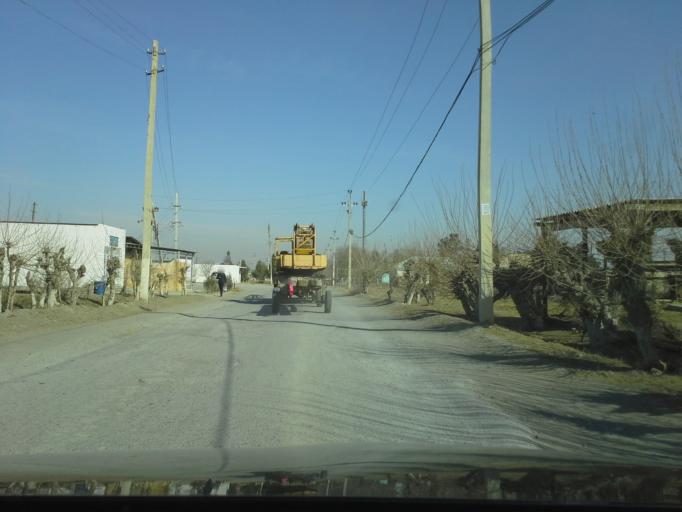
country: TM
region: Ahal
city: Abadan
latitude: 38.1229
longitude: 57.9968
